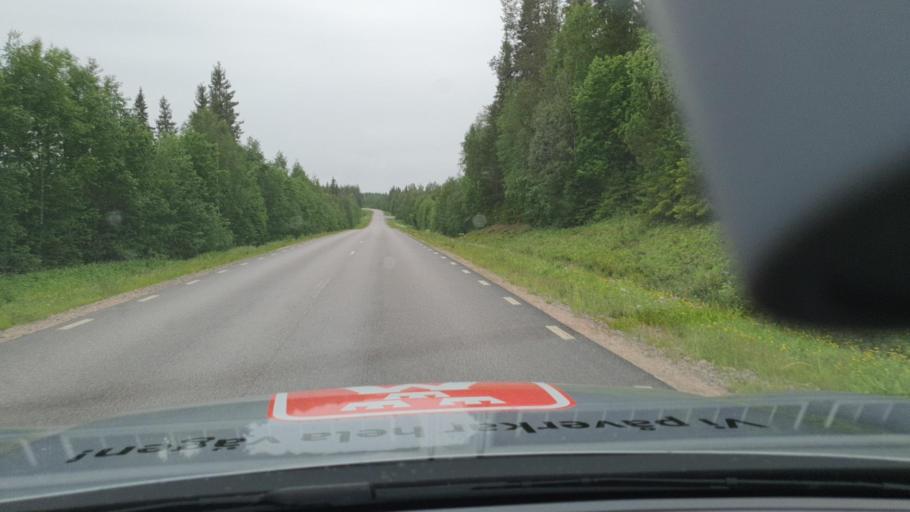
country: SE
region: Norrbotten
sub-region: Overtornea Kommun
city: OEvertornea
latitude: 66.4038
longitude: 23.4838
